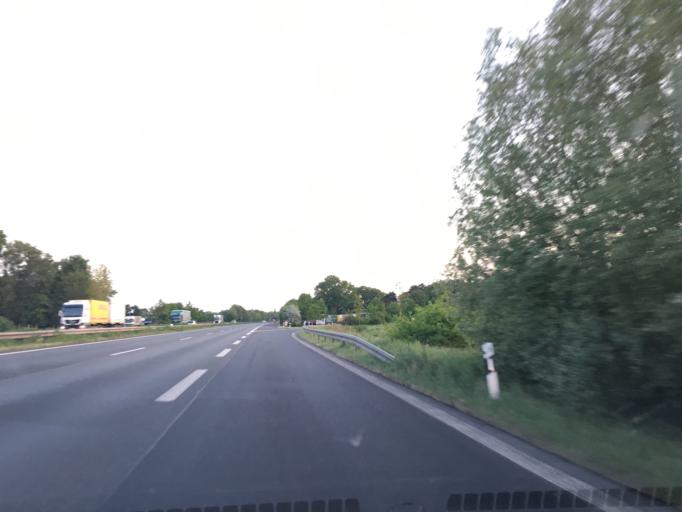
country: DE
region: North Rhine-Westphalia
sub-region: Regierungsbezirk Munster
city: Greven
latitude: 52.0342
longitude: 7.6039
